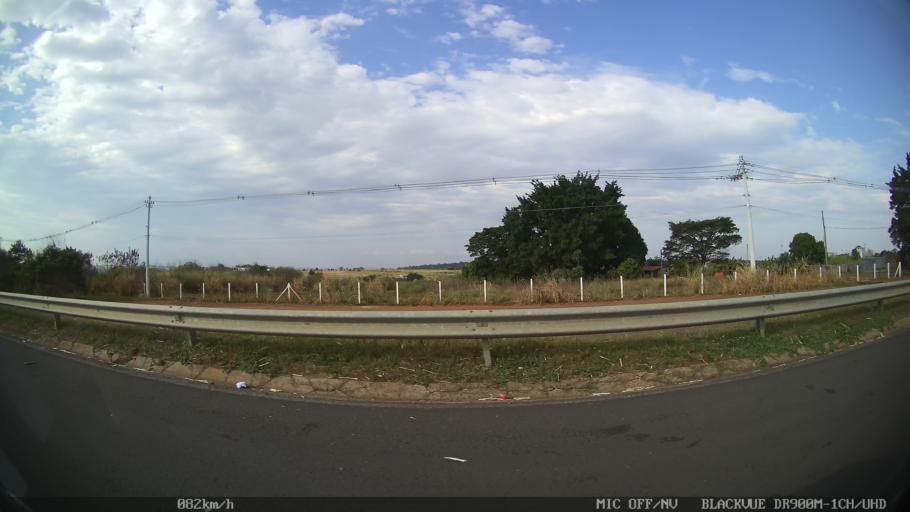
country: BR
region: Sao Paulo
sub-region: Paulinia
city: Paulinia
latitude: -22.7073
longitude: -47.1429
